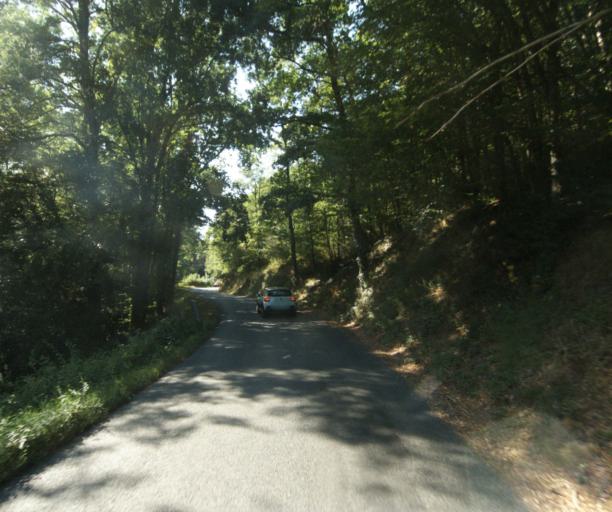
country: FR
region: Rhone-Alpes
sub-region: Departement du Rhone
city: Saint-Pierre-la-Palud
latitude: 45.7898
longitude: 4.6019
